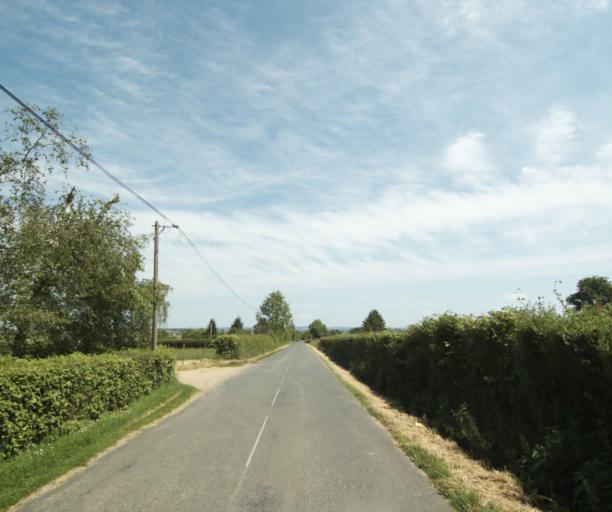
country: FR
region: Bourgogne
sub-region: Departement de Saone-et-Loire
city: Perrecy-les-Forges
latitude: 46.5771
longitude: 4.1413
